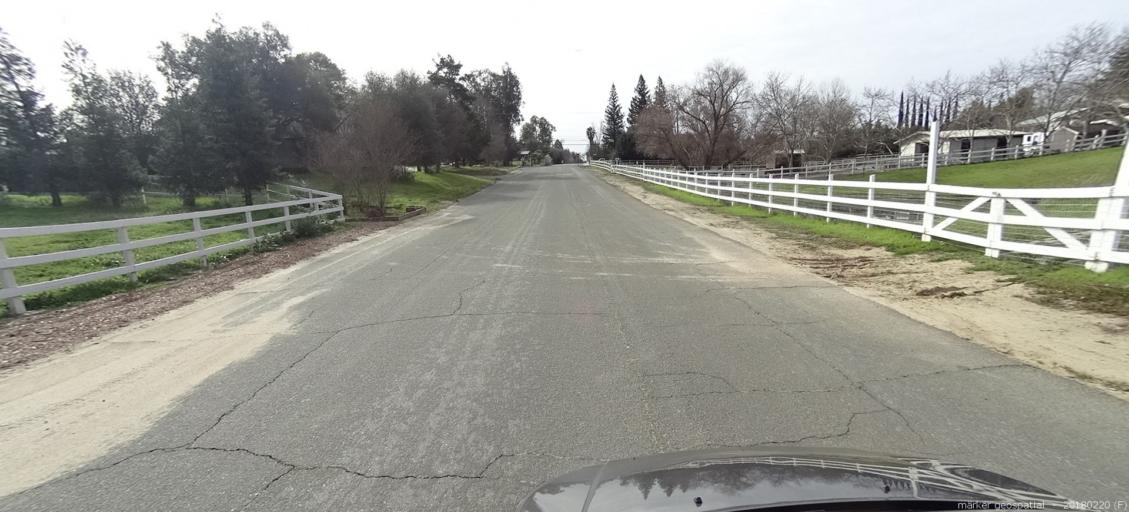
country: US
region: California
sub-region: Sacramento County
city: Orangevale
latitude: 38.7018
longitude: -121.2301
